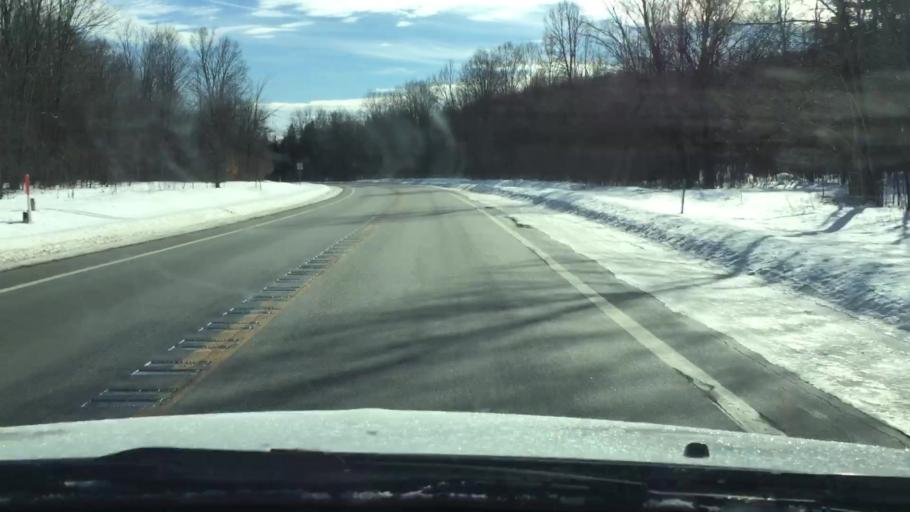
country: US
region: Michigan
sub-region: Antrim County
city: Mancelona
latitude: 45.0094
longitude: -85.0648
